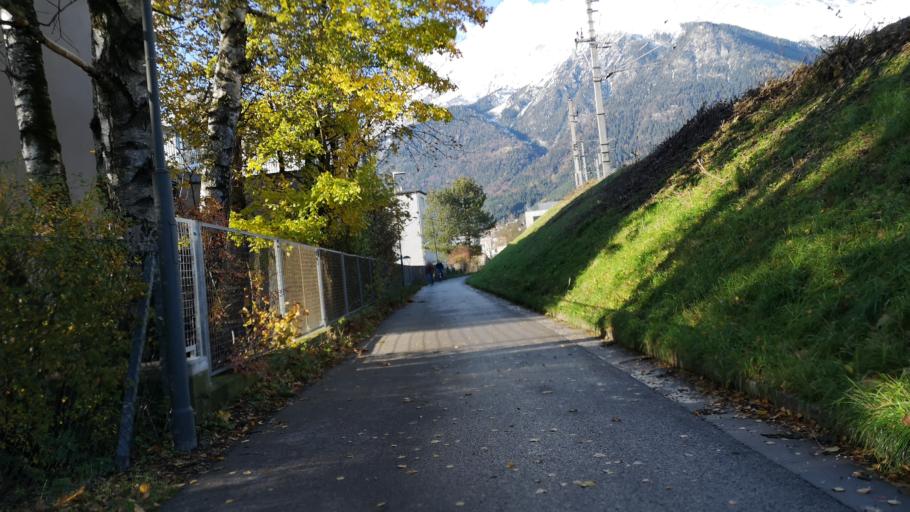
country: AT
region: Tyrol
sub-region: Innsbruck Stadt
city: Innsbruck
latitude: 47.2574
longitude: 11.3759
